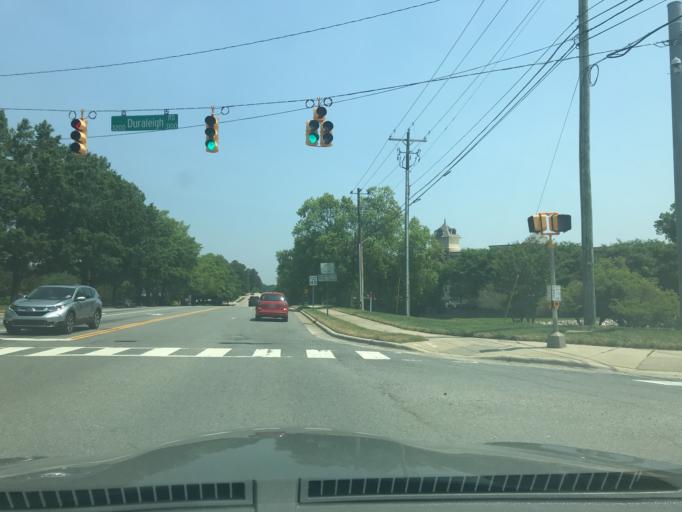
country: US
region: North Carolina
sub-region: Wake County
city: West Raleigh
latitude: 35.8238
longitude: -78.7069
